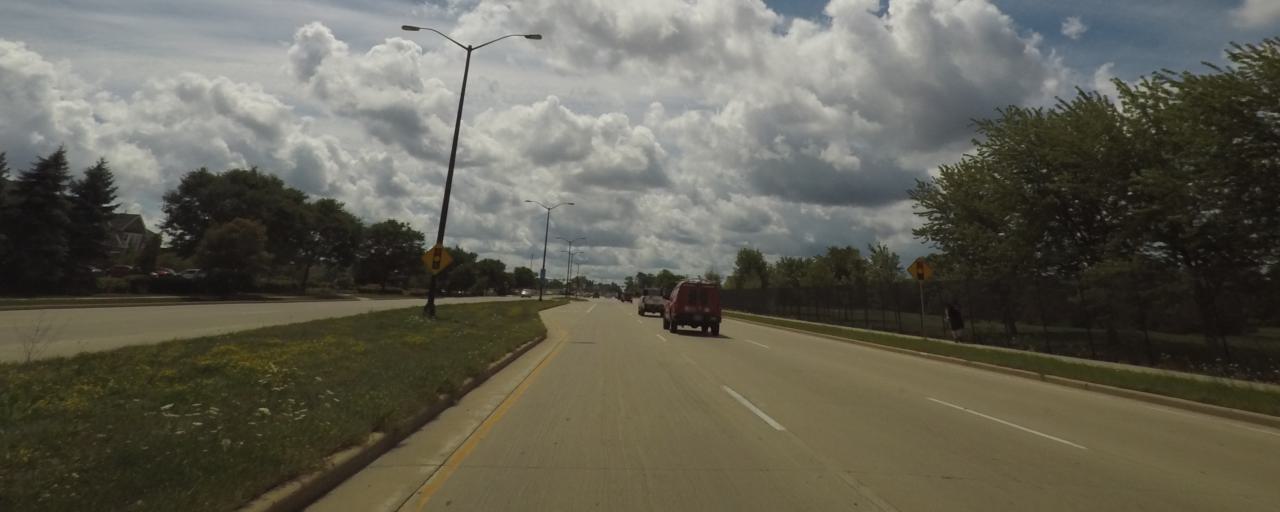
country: US
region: Wisconsin
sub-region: Waukesha County
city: Elm Grove
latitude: 43.0198
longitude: -88.1072
